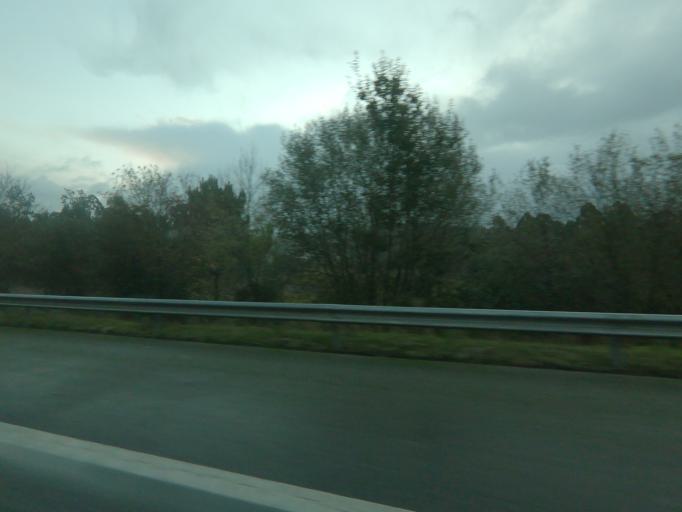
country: PT
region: Braga
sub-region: Barcelos
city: Galegos
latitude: 41.6437
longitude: -8.5550
